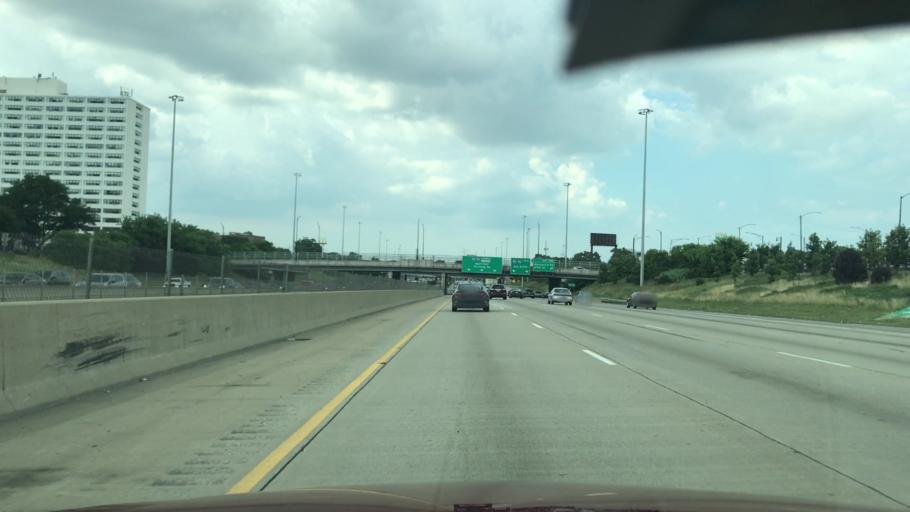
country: US
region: Illinois
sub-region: Cook County
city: Evergreen Park
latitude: 41.7635
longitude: -87.6255
